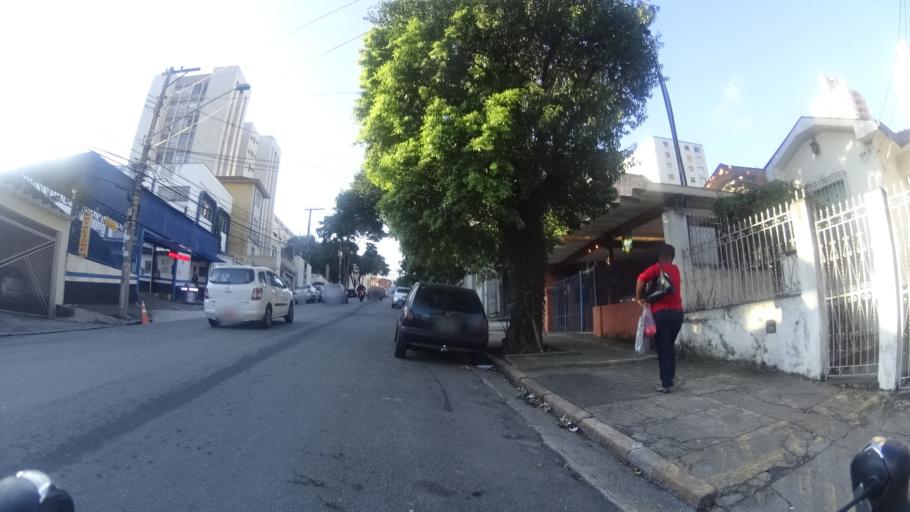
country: BR
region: Sao Paulo
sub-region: Sao Paulo
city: Sao Paulo
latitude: -23.5022
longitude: -46.6316
